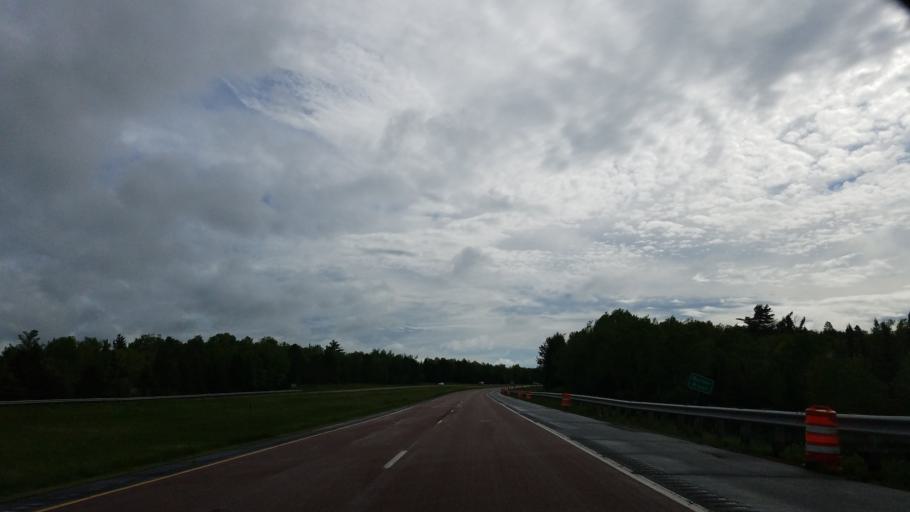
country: US
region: Minnesota
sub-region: Lake County
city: Two Harbors
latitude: 46.9252
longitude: -91.8561
